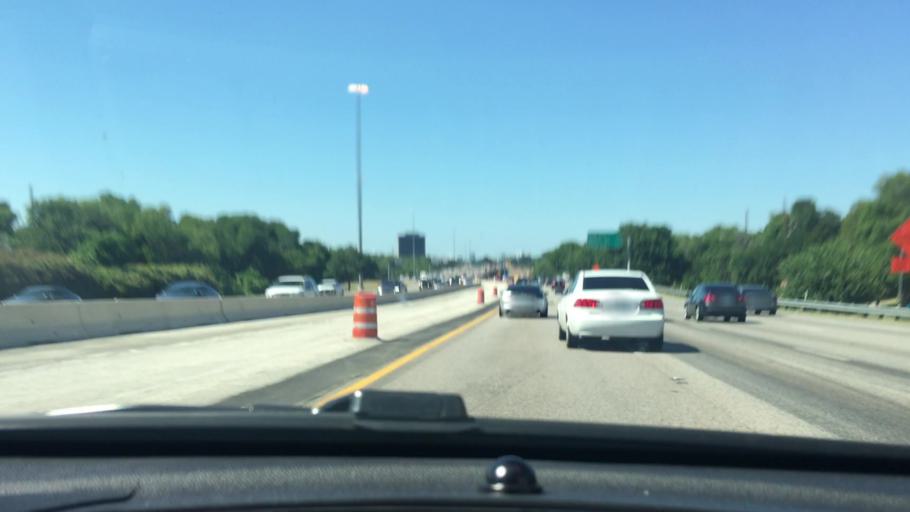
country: US
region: Texas
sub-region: Dallas County
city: Dallas
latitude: 32.7258
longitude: -96.8260
